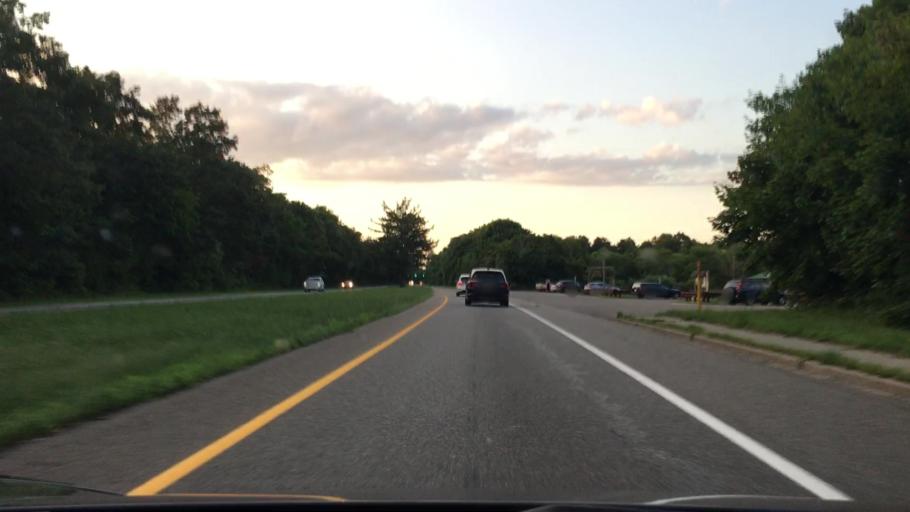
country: US
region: New York
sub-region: Suffolk County
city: Deer Park
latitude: 40.7757
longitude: -73.3104
